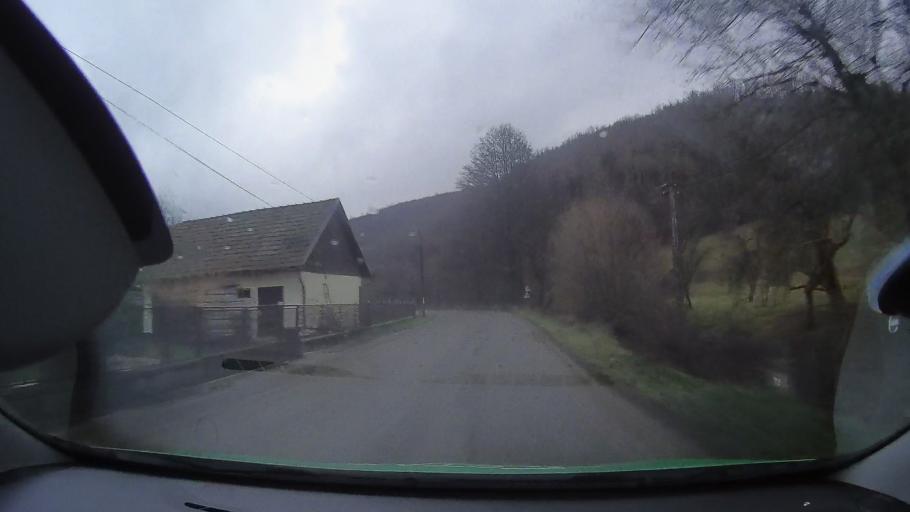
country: RO
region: Hunedoara
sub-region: Comuna Baia de Cris
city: Baia de Cris
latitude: 46.2106
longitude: 22.7160
